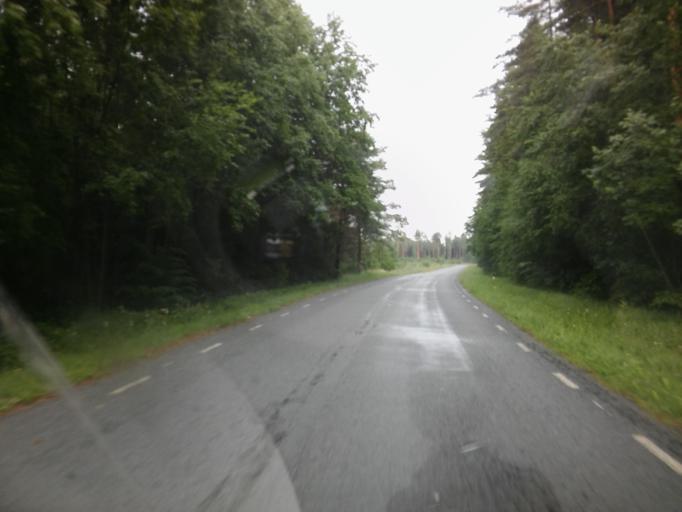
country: EE
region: Raplamaa
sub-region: Maerjamaa vald
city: Marjamaa
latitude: 58.7683
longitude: 24.4391
